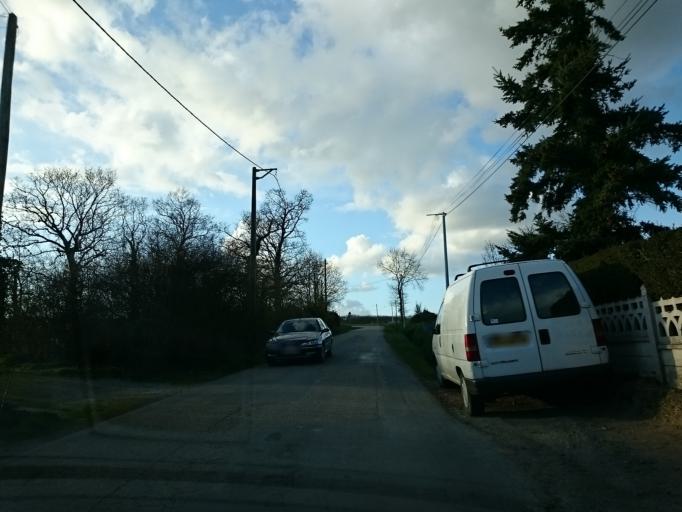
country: FR
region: Brittany
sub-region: Departement d'Ille-et-Vilaine
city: Crevin
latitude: 47.9264
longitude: -1.6627
